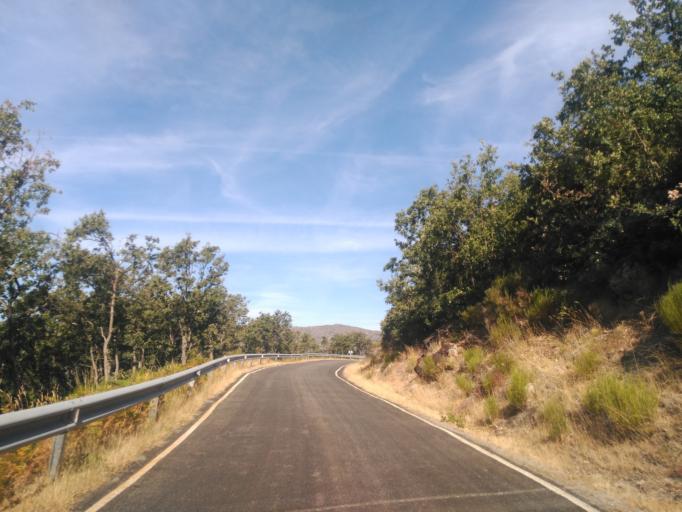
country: ES
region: Castille and Leon
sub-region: Provincia de Zamora
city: Cobreros
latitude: 42.1330
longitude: -6.7343
